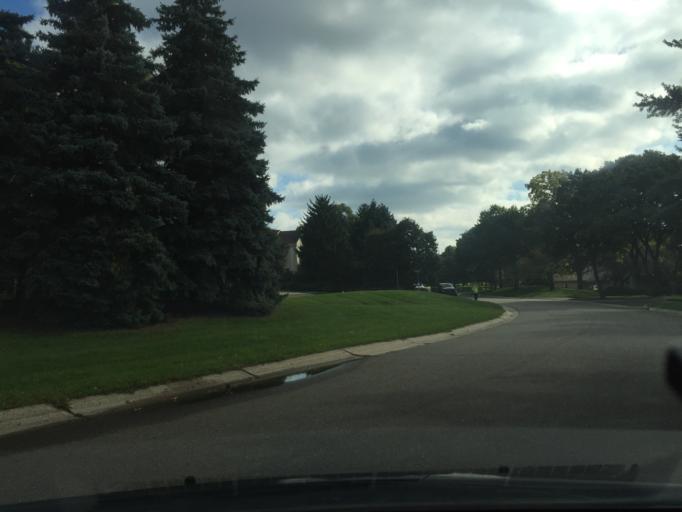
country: US
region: Michigan
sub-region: Oakland County
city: Sylvan Lake
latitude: 42.5813
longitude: -83.3184
